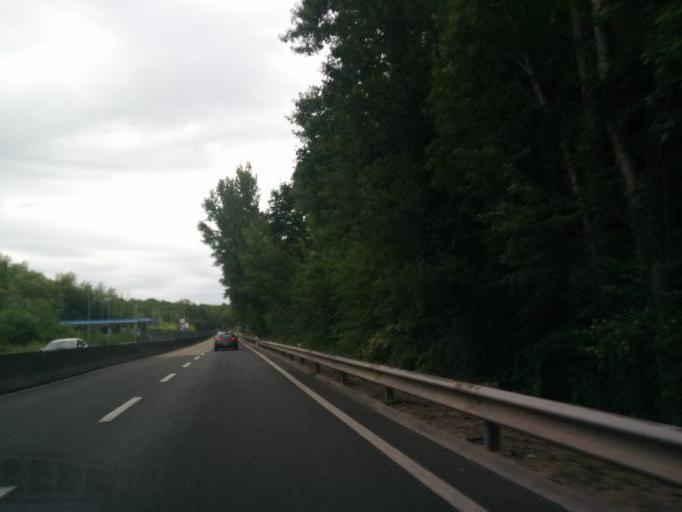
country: IT
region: Tuscany
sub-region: Provincia di Siena
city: Belverde
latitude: 43.3511
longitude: 11.3027
